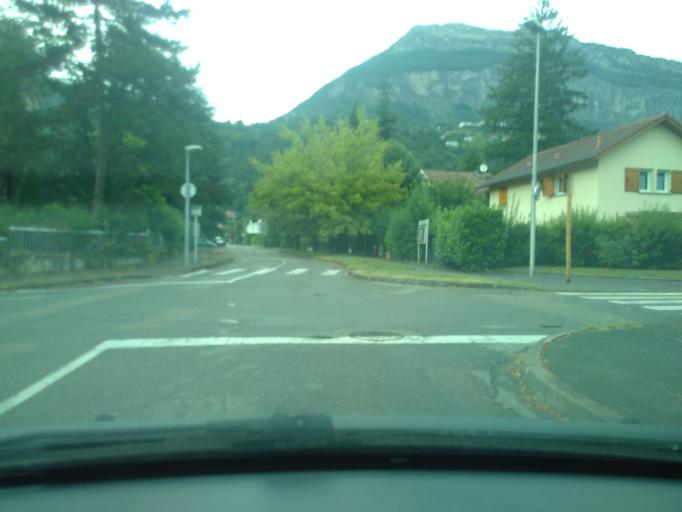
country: FR
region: Rhone-Alpes
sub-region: Departement de l'Isere
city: Corenc
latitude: 45.2100
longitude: 5.7674
